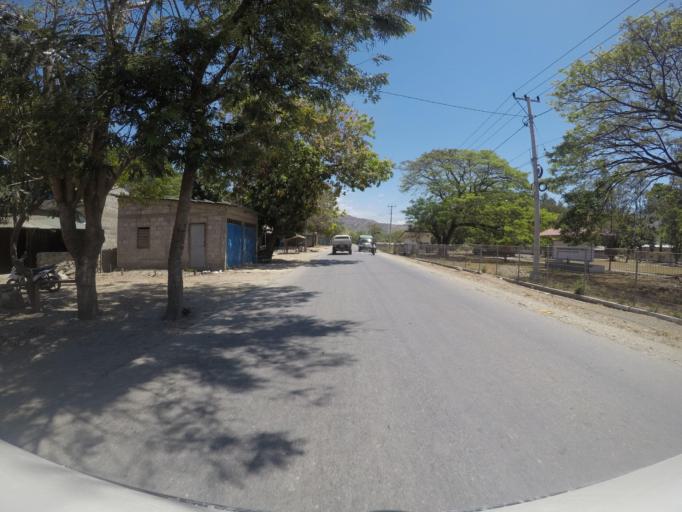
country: ID
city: Metinaro
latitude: -8.5519
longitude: 125.6610
